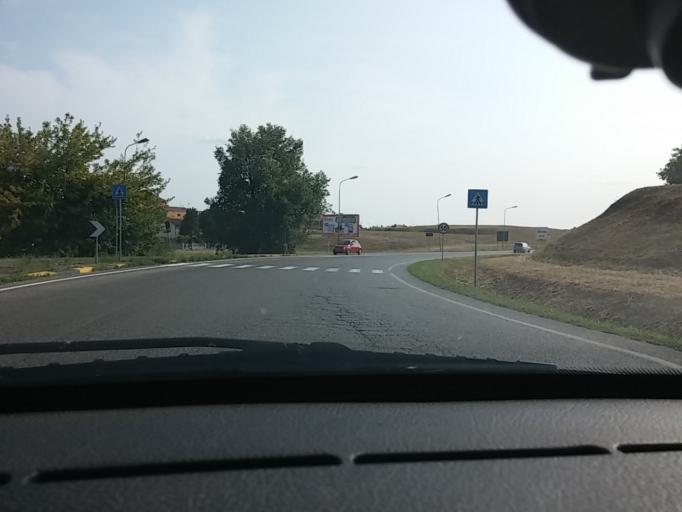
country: IT
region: Emilia-Romagna
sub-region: Provincia di Ferrara
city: Ferrara
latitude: 44.8347
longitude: 11.6011
